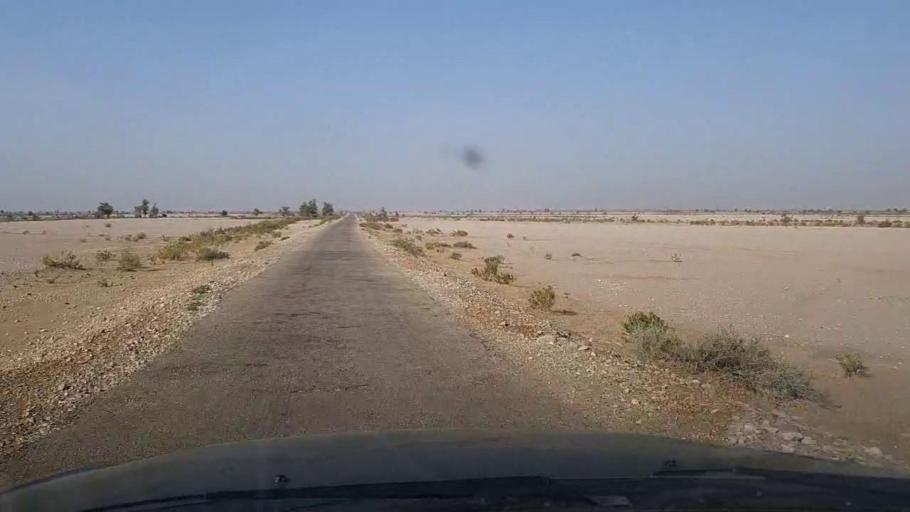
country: PK
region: Sindh
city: Sann
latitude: 25.9912
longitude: 68.0700
